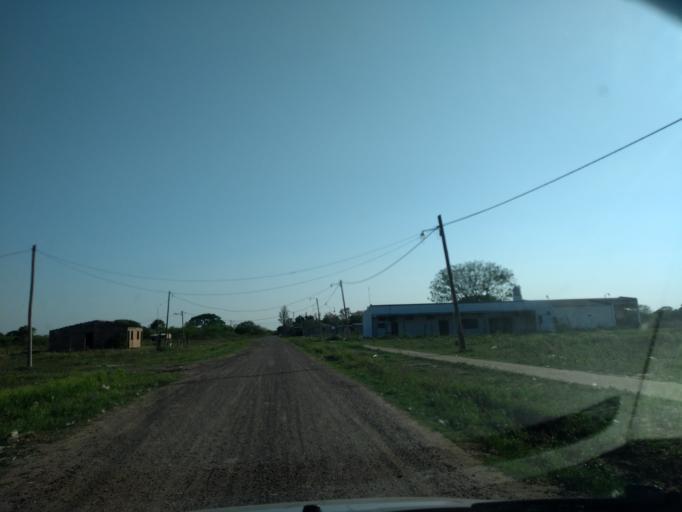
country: AR
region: Chaco
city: Fontana
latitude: -27.4143
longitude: -59.0574
